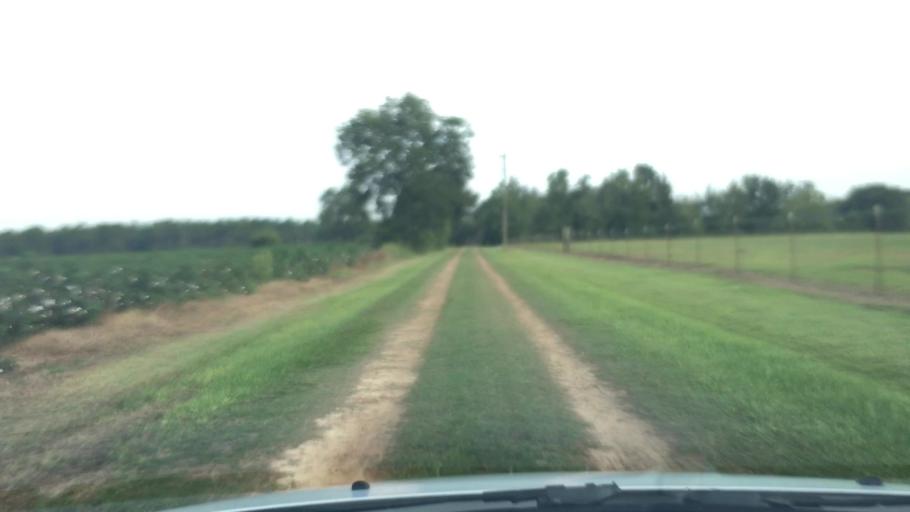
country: US
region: Georgia
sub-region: Grady County
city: Cairo
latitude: 30.8245
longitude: -84.2412
